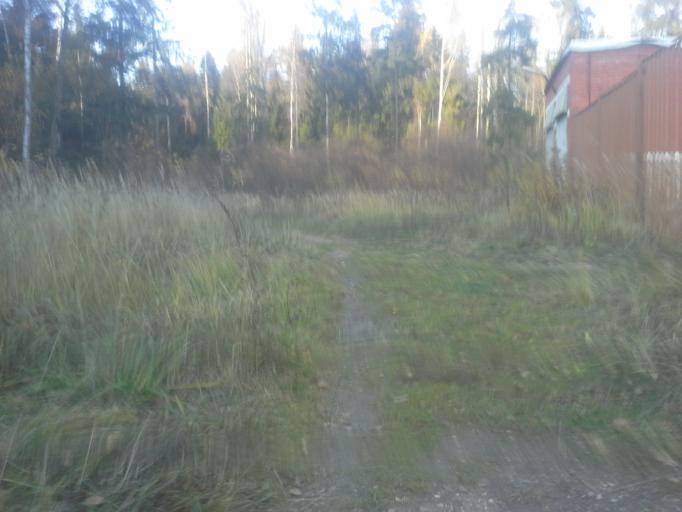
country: RU
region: Moskovskaya
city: Krasnoznamensk
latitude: 55.5833
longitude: 37.0182
